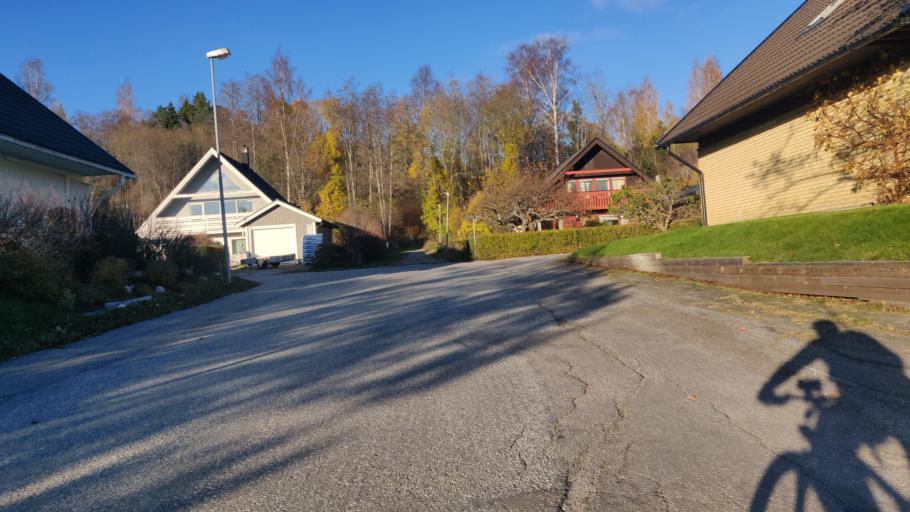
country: SE
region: Vaesternorrland
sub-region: Sundsvalls Kommun
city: Nolby
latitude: 62.2741
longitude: 17.3696
